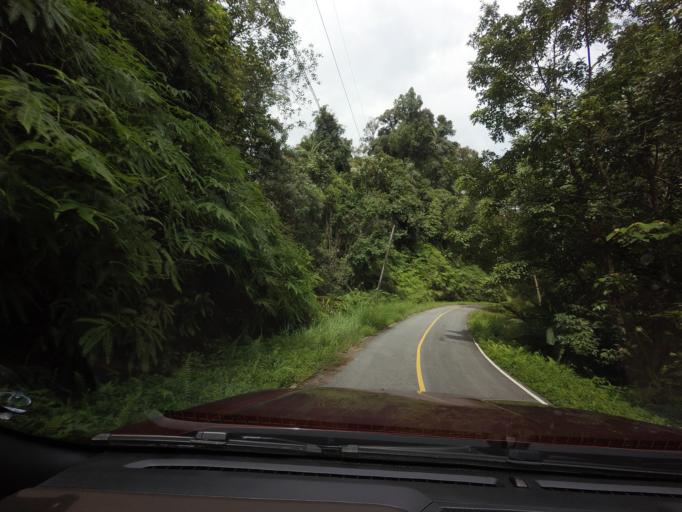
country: TH
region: Narathiwat
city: Sukhirin
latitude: 5.9370
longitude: 101.6513
